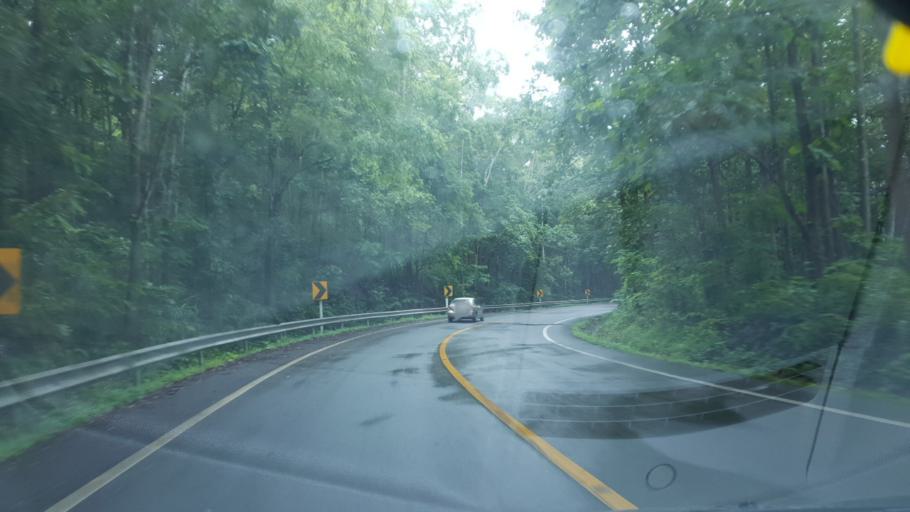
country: TH
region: Mae Hong Son
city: Pa Pae
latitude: 18.2203
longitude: 97.9419
